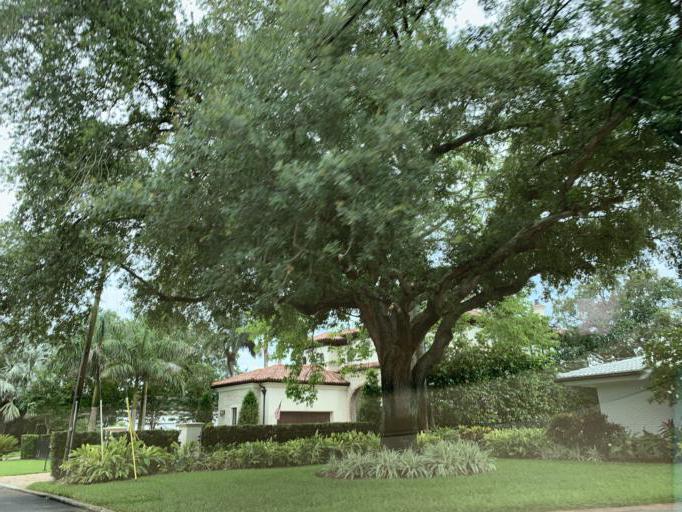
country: US
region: Florida
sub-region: Pinellas County
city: Saint Petersburg
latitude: 27.7909
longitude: -82.6126
